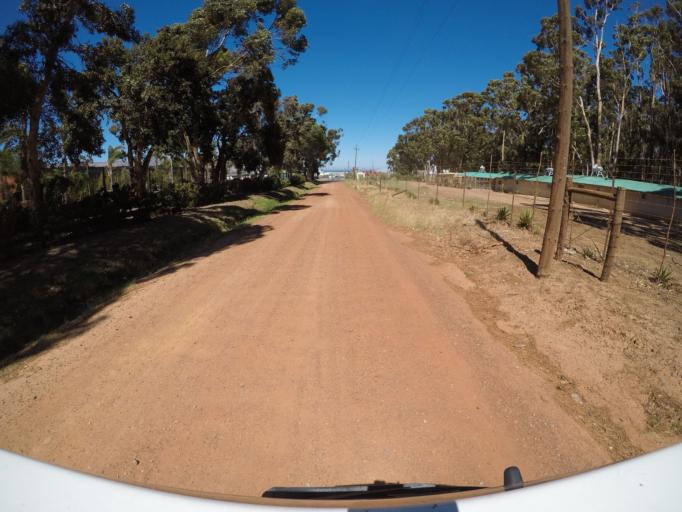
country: ZA
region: Western Cape
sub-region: Overberg District Municipality
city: Grabouw
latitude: -34.1162
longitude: 18.8781
